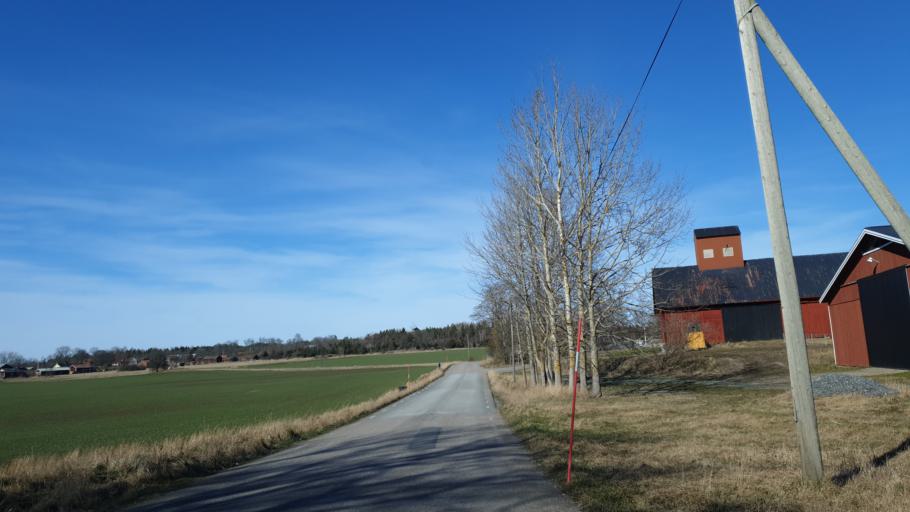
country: SE
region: Uppsala
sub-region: Enkopings Kommun
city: Dalby
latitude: 59.5184
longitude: 17.2826
